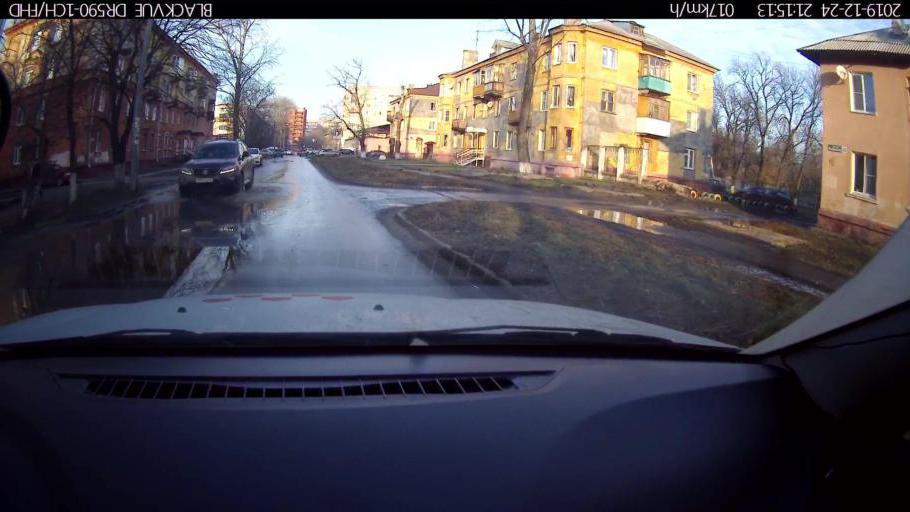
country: RU
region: Nizjnij Novgorod
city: Nizhniy Novgorod
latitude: 56.2648
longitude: 43.8870
